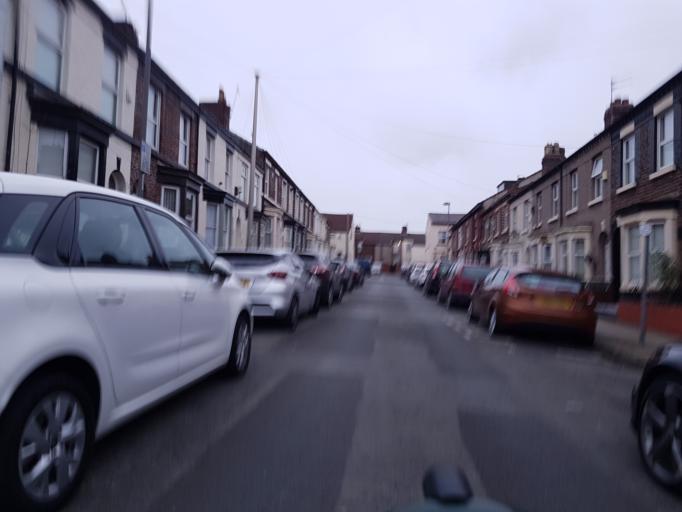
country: GB
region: England
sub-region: Sefton
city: Litherland
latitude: 53.4485
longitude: -2.9677
